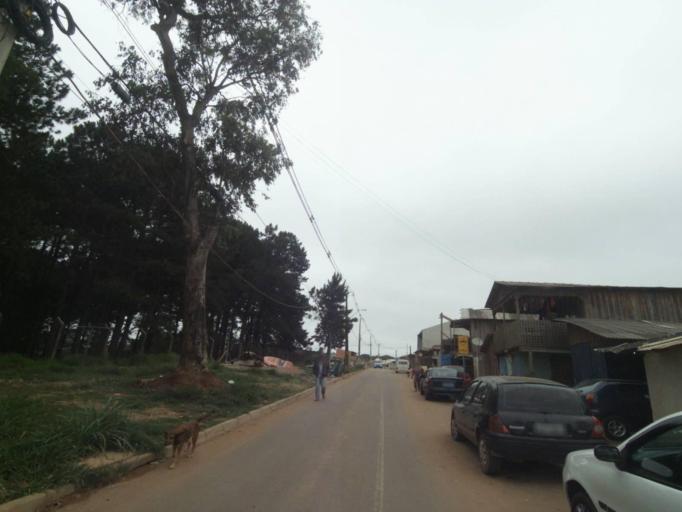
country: BR
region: Parana
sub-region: Araucaria
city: Araucaria
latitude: -25.5072
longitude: -49.3513
